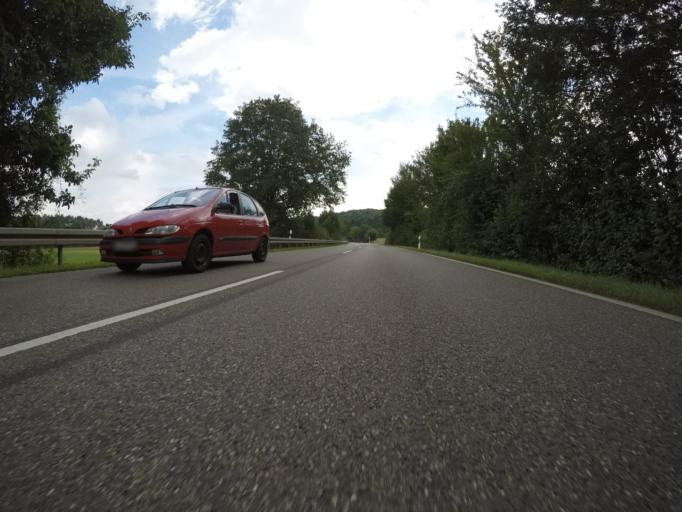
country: DE
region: Baden-Wuerttemberg
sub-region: Regierungsbezirk Stuttgart
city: Oberriexingen
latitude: 48.9221
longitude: 9.0160
